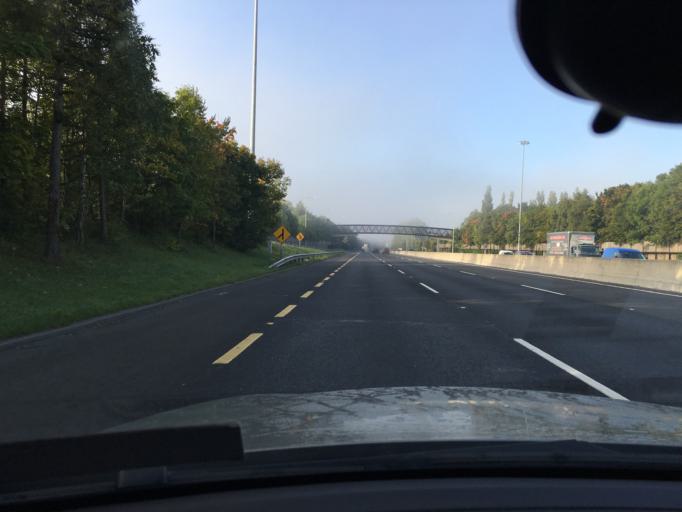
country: IE
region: Leinster
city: Lucan
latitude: 53.3564
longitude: -6.4271
